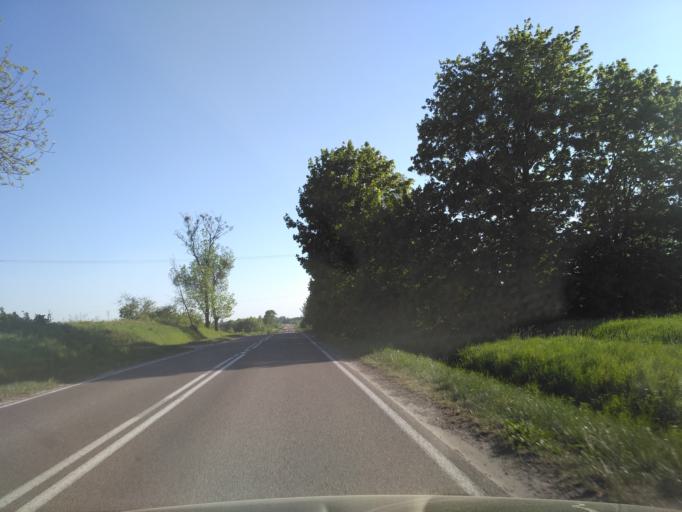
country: PL
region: Lublin Voivodeship
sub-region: Powiat swidnicki
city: Trawniki
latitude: 51.2042
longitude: 23.0673
